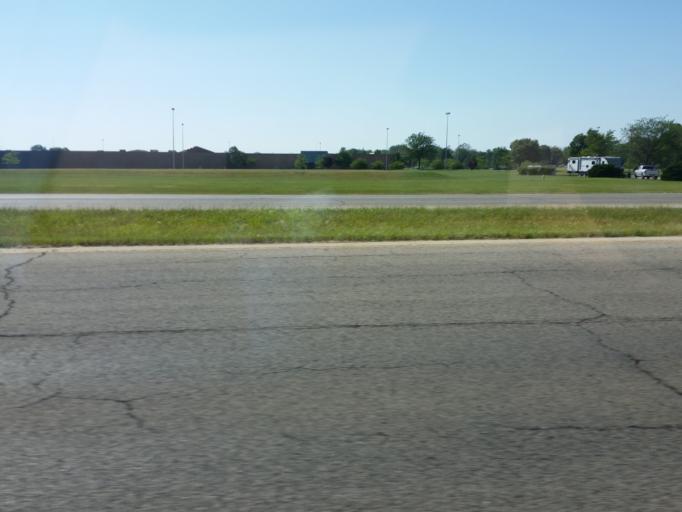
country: US
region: Illinois
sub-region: Winnebago County
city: Machesney Park
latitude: 42.3501
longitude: -89.0484
